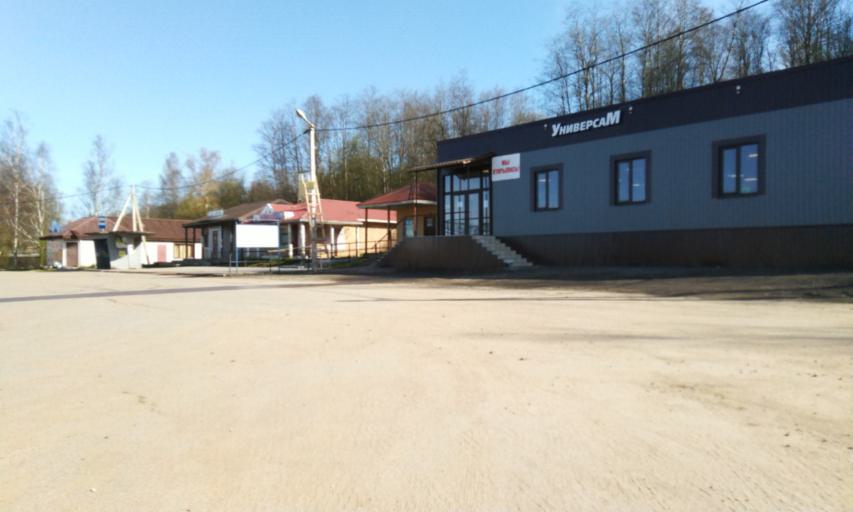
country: RU
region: Leningrad
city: Leskolovo
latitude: 60.3185
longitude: 30.4316
